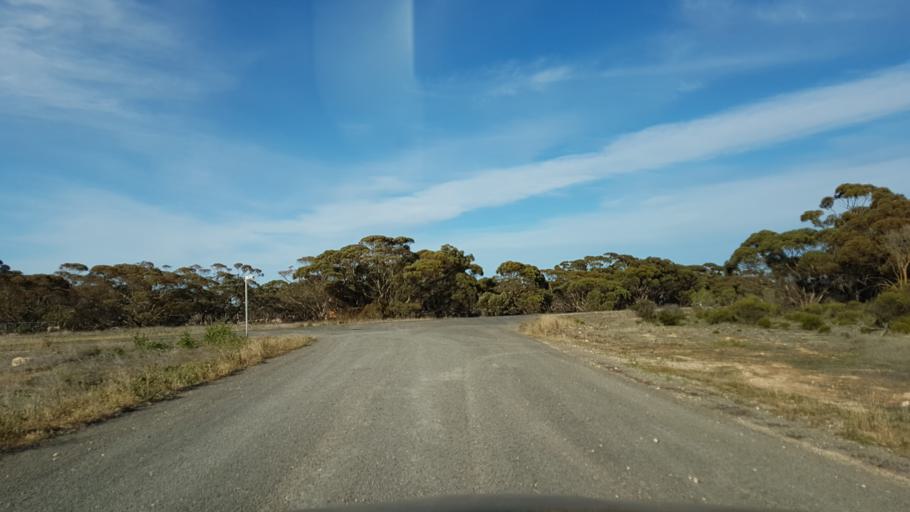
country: AU
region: South Australia
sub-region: Mid Murray
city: Mannum
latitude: -34.9851
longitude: 139.5737
